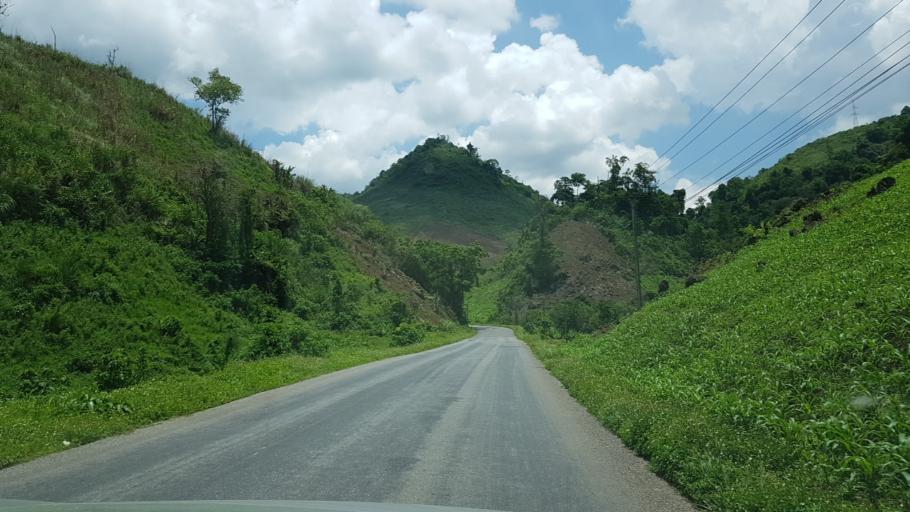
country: LA
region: Vientiane
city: Muang Kasi
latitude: 19.1364
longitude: 102.2886
